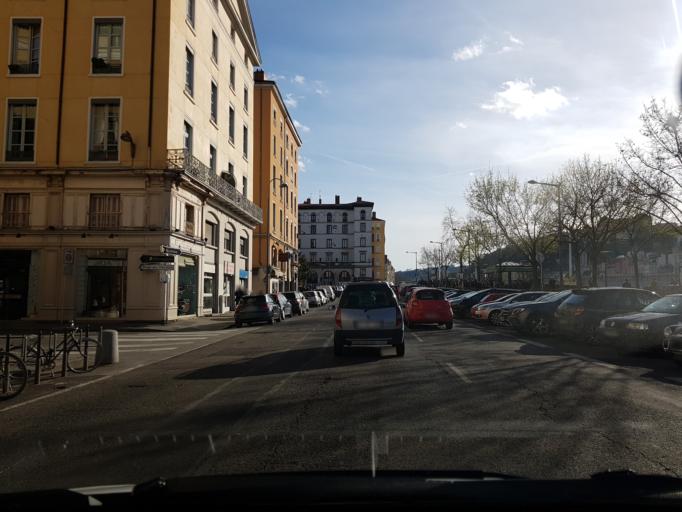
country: FR
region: Rhone-Alpes
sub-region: Departement du Rhone
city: Lyon
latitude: 45.7602
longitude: 4.8306
